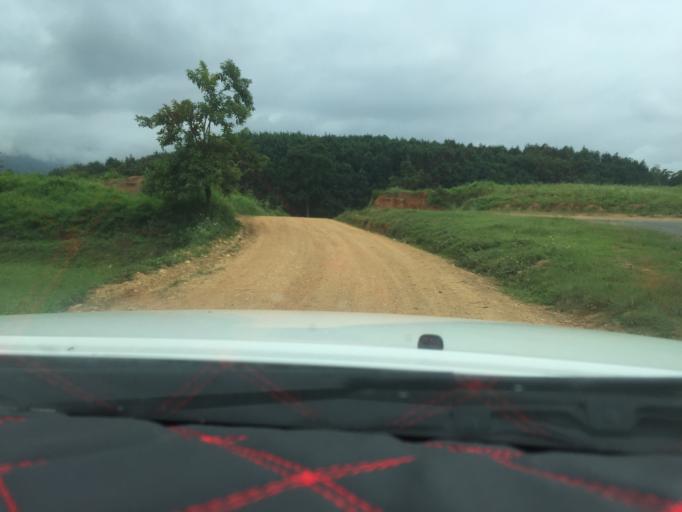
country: TH
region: Phayao
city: Phu Sang
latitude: 19.6942
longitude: 100.5011
